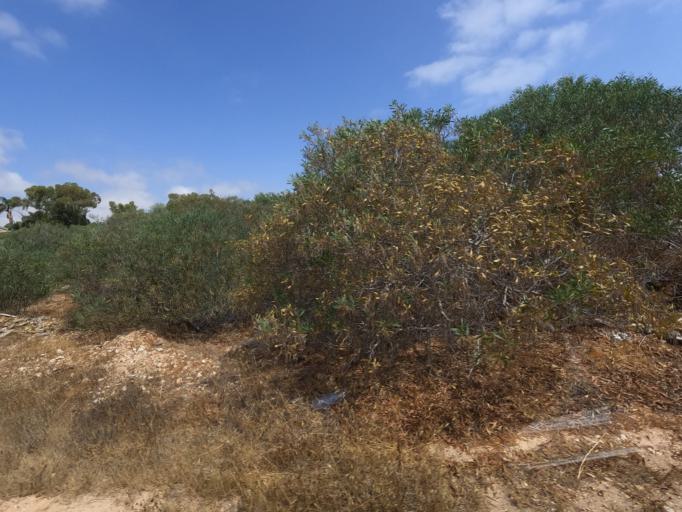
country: CY
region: Ammochostos
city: Protaras
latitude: 35.0047
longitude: 34.0515
